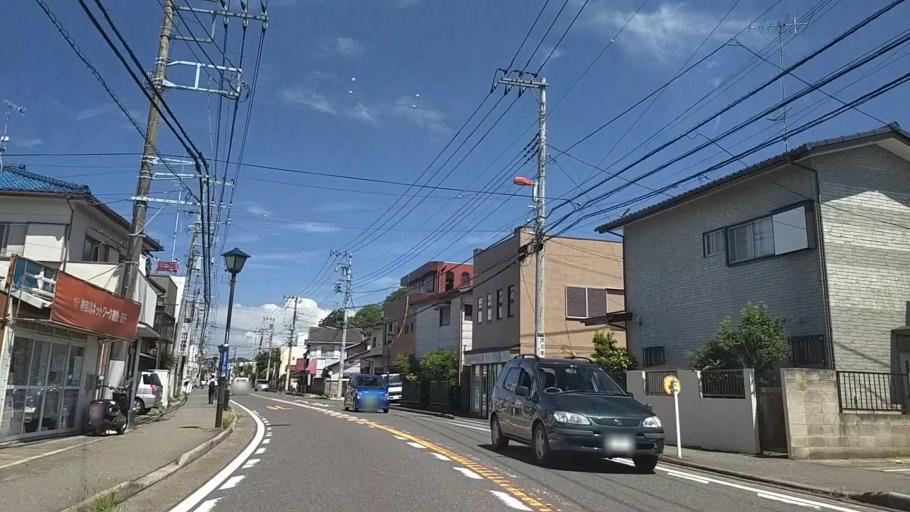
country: JP
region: Kanagawa
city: Zushi
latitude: 35.2951
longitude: 139.5871
